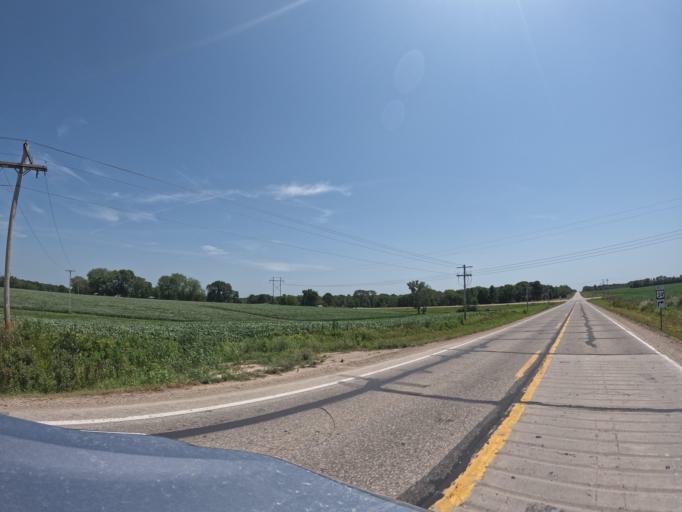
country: US
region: Iowa
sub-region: Henry County
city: Mount Pleasant
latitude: 40.9689
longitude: -91.6124
